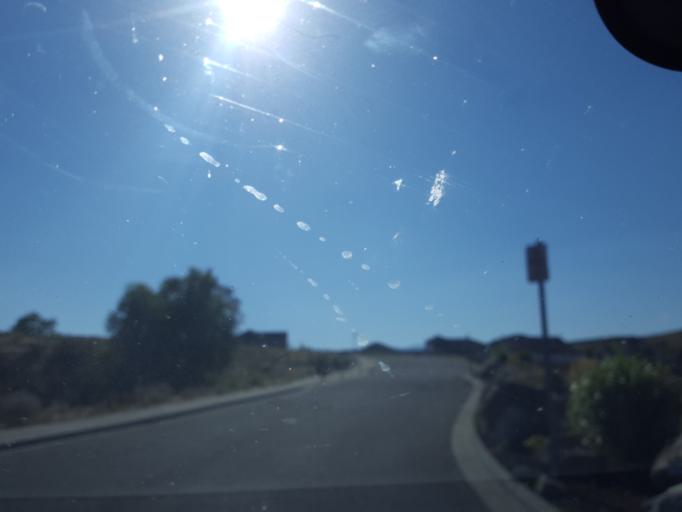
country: US
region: Washington
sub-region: Chelan County
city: Chelan
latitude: 47.8418
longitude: -119.9959
